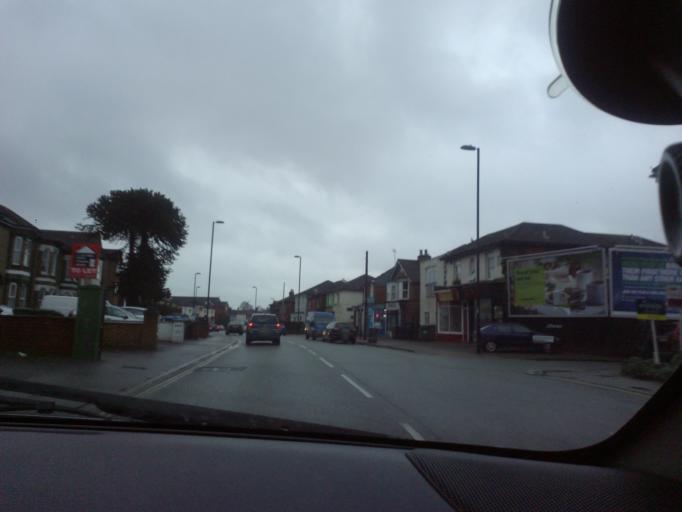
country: GB
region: England
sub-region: Southampton
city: Southampton
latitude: 50.9131
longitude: -1.4218
